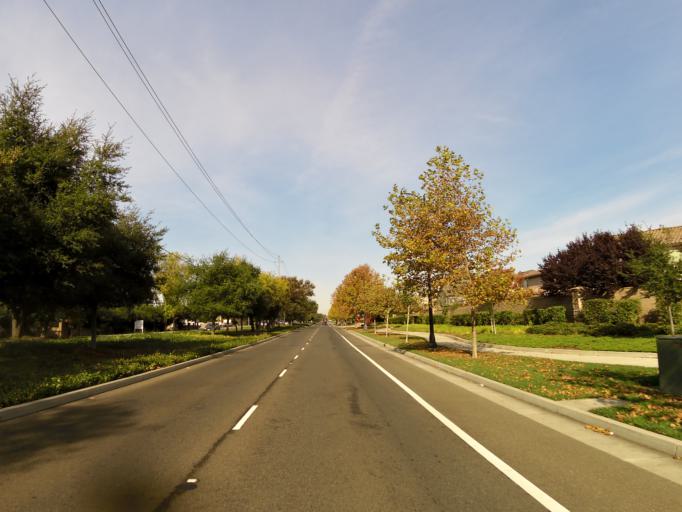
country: US
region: California
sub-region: Sacramento County
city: Laguna
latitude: 38.4000
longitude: -121.4176
